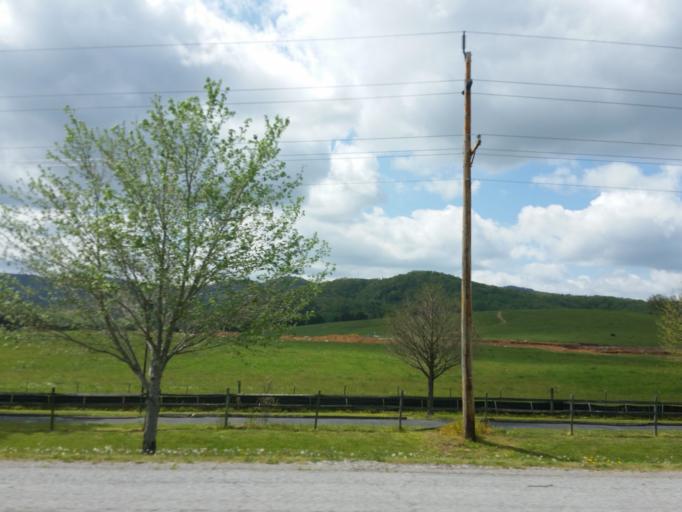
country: US
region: Tennessee
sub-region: Claiborne County
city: Harrogate
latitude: 36.5637
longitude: -83.6573
